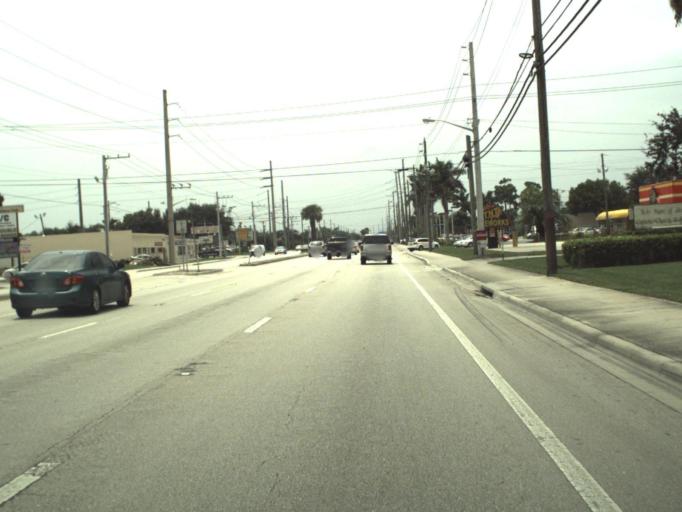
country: US
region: Florida
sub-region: Palm Beach County
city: Royal Palm Estates
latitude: 26.6724
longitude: -80.1124
